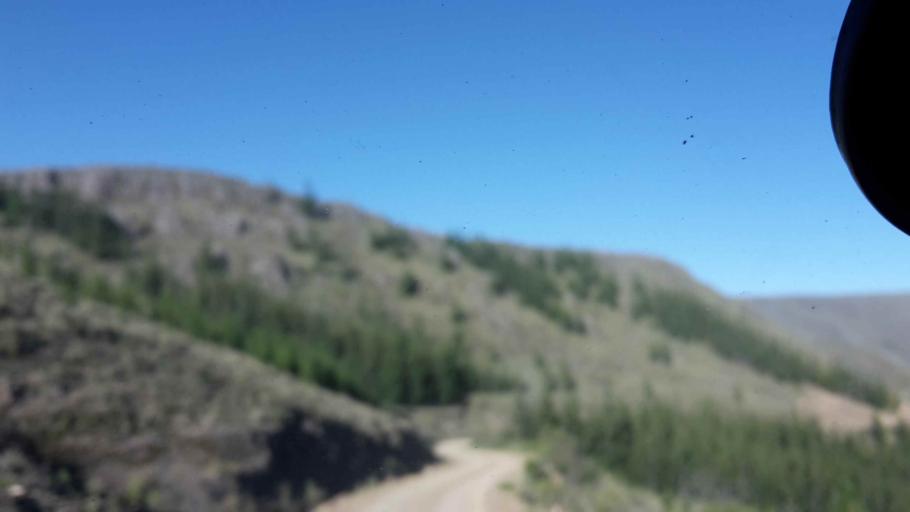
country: BO
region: Cochabamba
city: Arani
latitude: -17.7264
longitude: -65.6370
